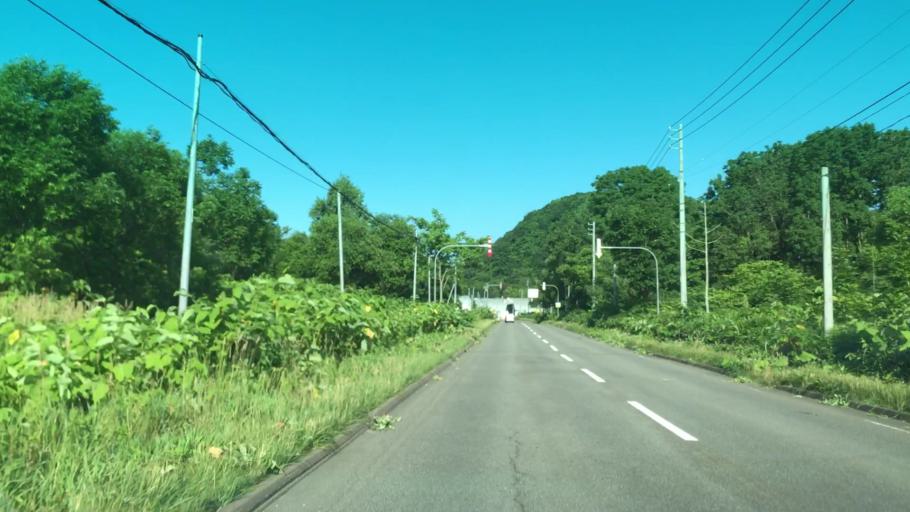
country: JP
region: Hokkaido
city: Otaru
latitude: 43.0889
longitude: 140.9293
